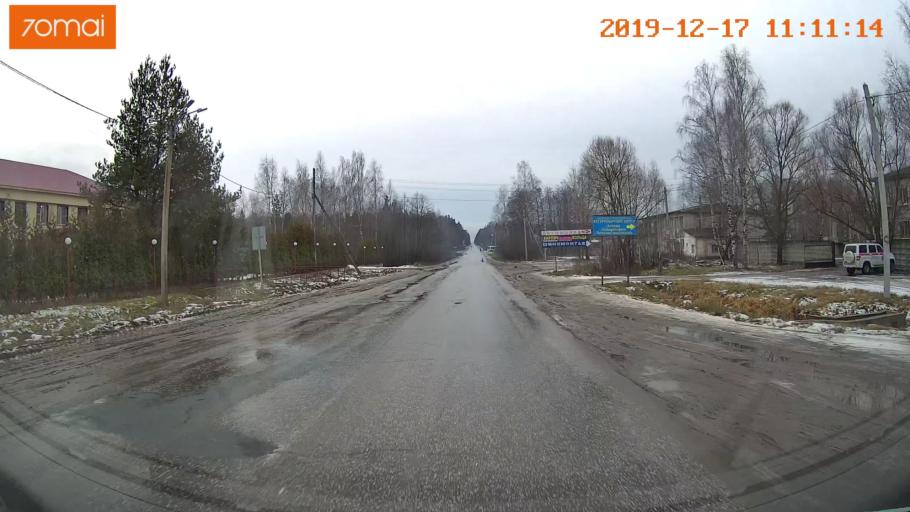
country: RU
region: Vladimir
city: Gus'-Khrustal'nyy
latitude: 55.5880
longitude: 40.6379
